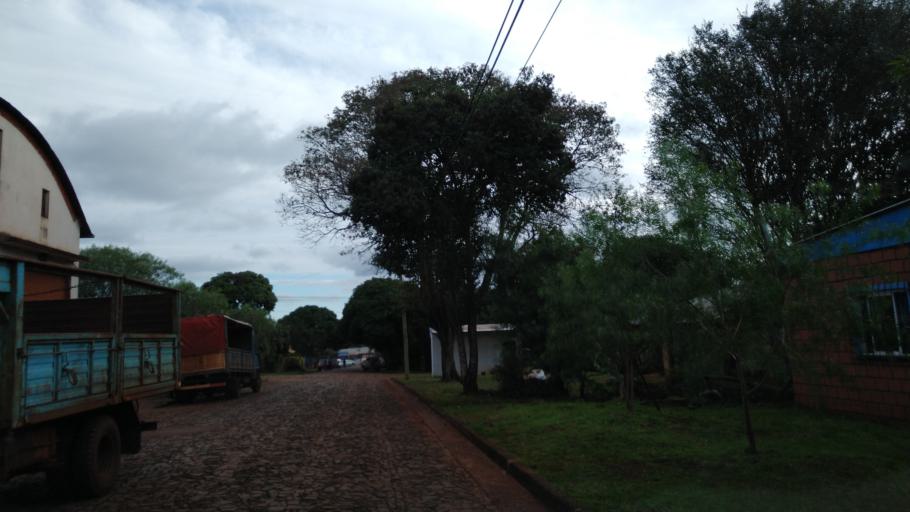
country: AR
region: Misiones
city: Jardin America
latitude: -27.0448
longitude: -55.2421
